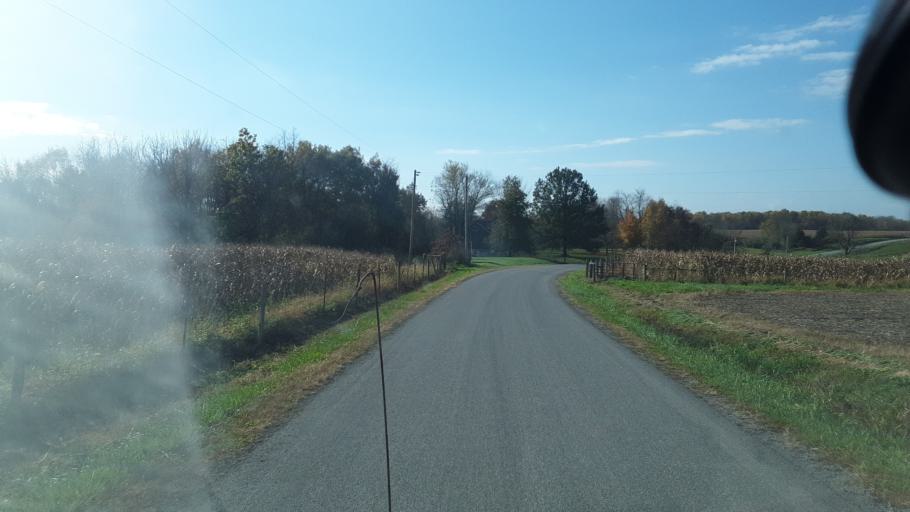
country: US
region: Ohio
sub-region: Highland County
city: Leesburg
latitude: 39.3182
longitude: -83.4936
